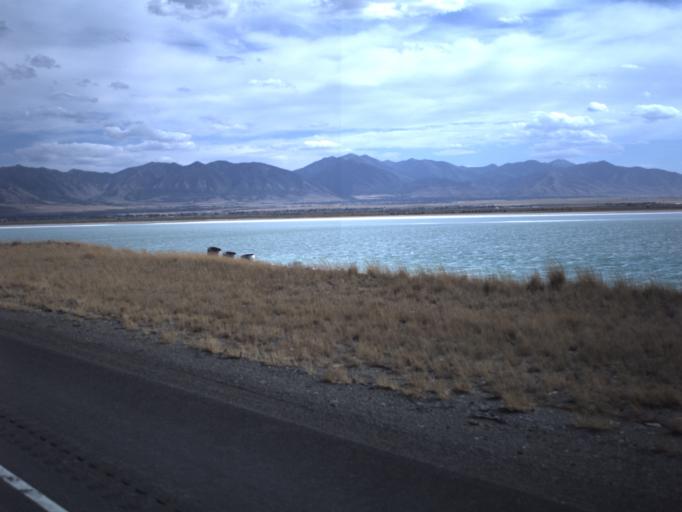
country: US
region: Utah
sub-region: Tooele County
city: Stansbury park
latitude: 40.6690
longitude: -112.3811
